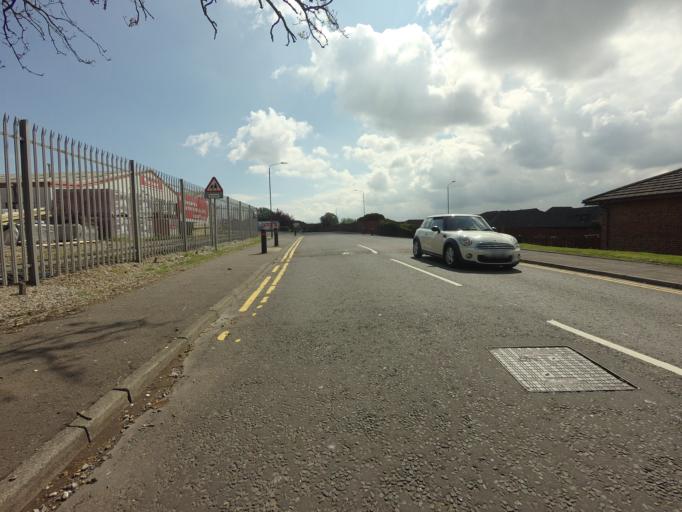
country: GB
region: Scotland
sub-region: Falkirk
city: Falkirk
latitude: 56.0246
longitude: -3.7927
